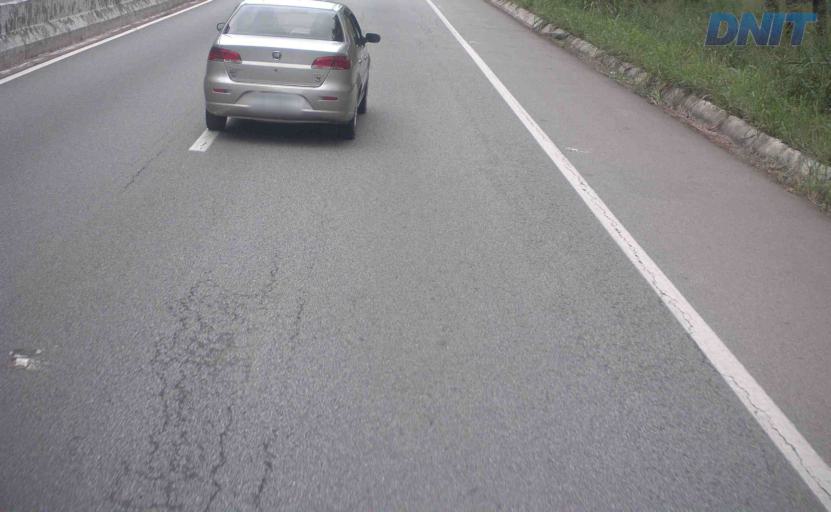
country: BR
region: Minas Gerais
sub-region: Nova Era
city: Nova Era
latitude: -19.7705
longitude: -43.0470
